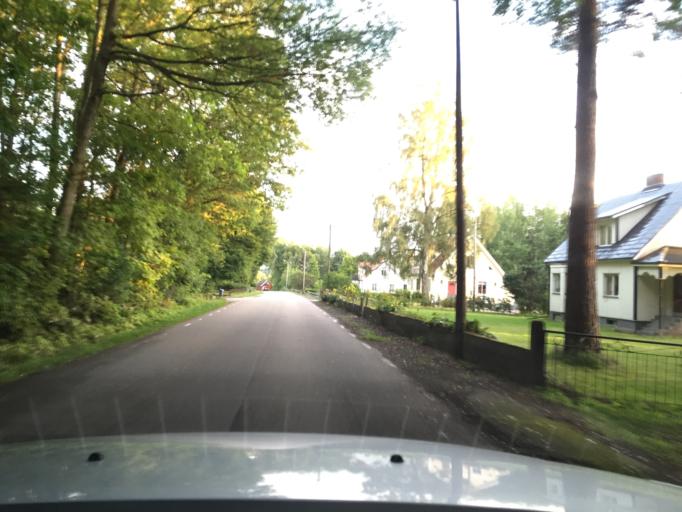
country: SE
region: Skane
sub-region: Hassleholms Kommun
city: Vinslov
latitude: 55.9994
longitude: 13.8179
